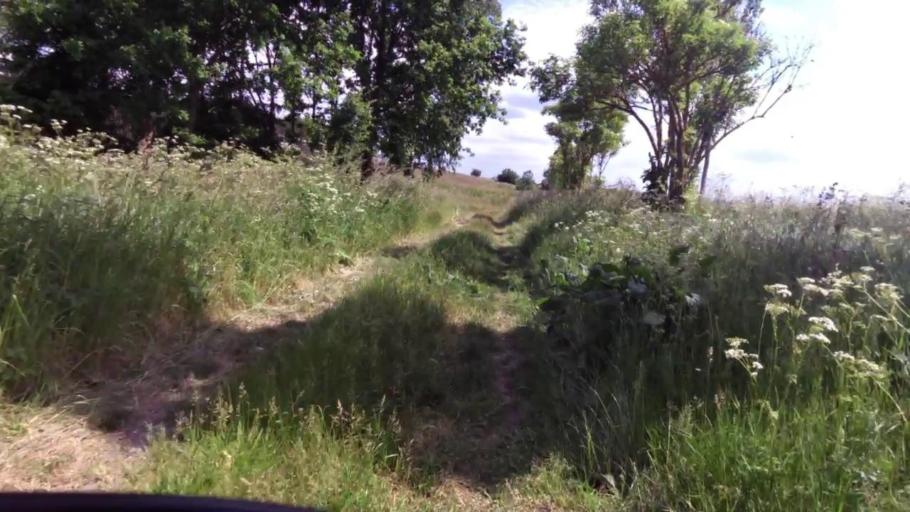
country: PL
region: West Pomeranian Voivodeship
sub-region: Powiat kamienski
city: Wolin
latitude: 53.8538
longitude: 14.5698
